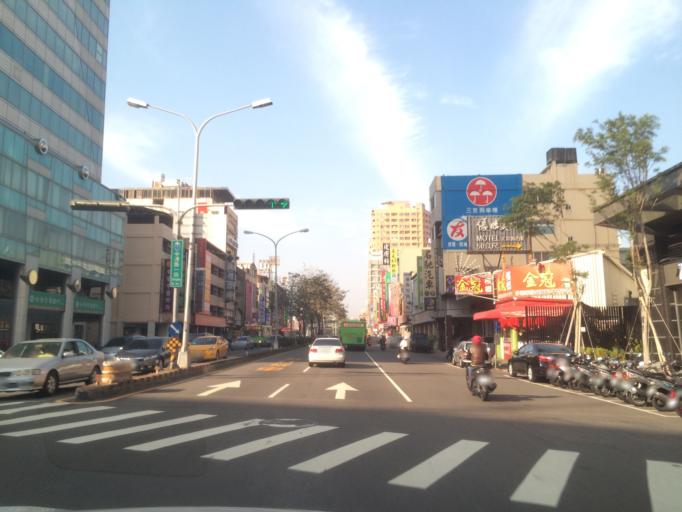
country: TW
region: Taiwan
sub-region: Taichung City
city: Taichung
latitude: 24.1652
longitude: 120.6739
